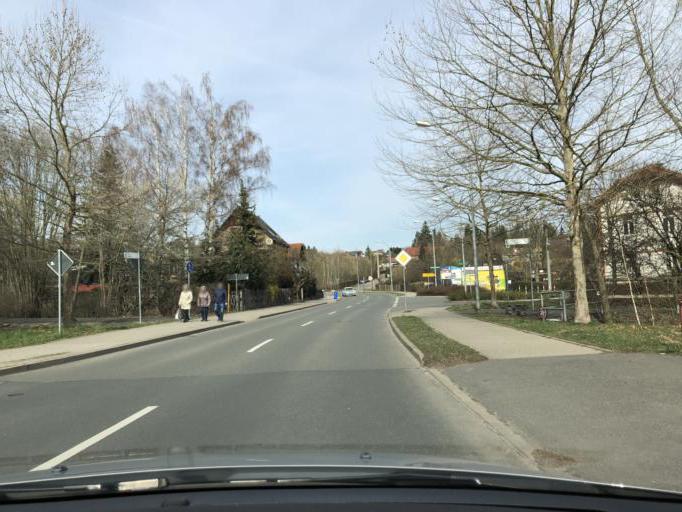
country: DE
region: Thuringia
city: Eisenberg
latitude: 50.9739
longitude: 11.9000
